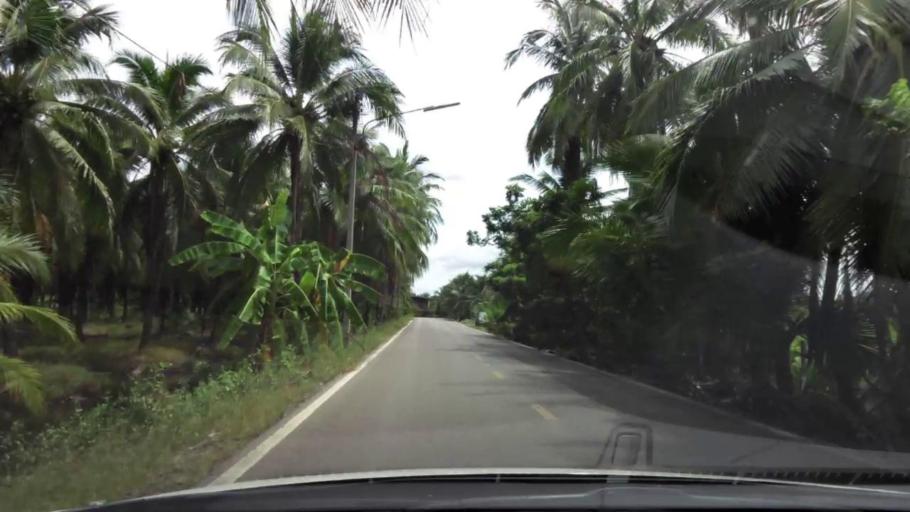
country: TH
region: Ratchaburi
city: Damnoen Saduak
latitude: 13.5251
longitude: 100.0160
